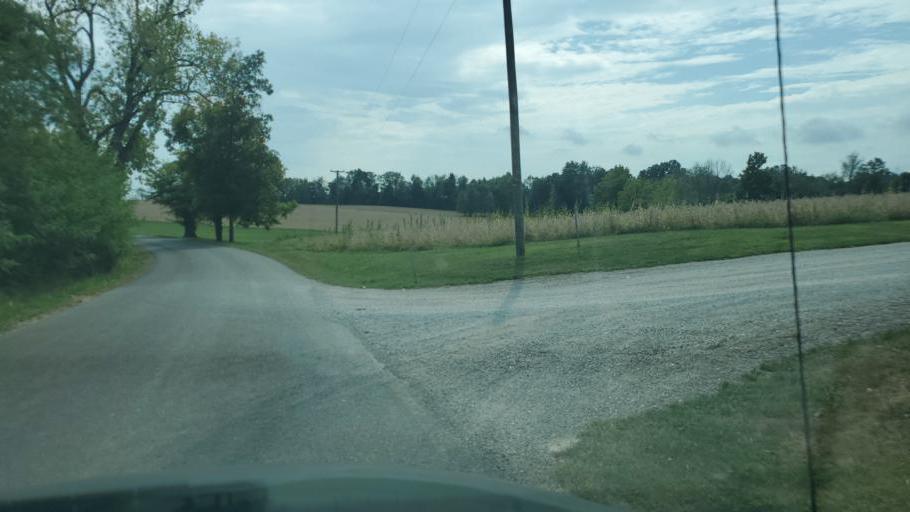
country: US
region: Ohio
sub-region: Muskingum County
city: Zanesville
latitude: 39.9693
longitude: -82.1583
